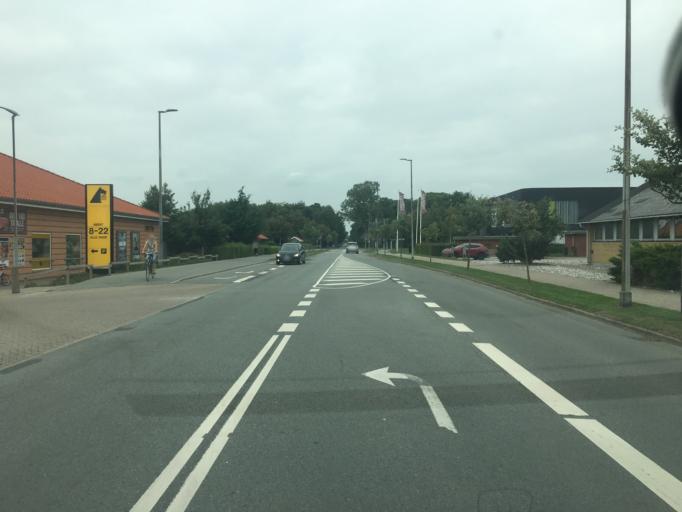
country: DK
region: South Denmark
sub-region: Tonder Kommune
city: Tonder
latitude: 54.9396
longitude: 8.8558
